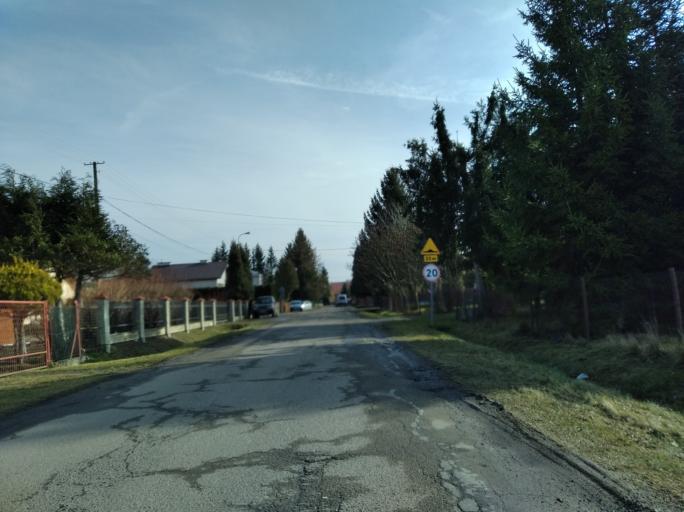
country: PL
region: Subcarpathian Voivodeship
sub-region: Powiat brzozowski
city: Humniska
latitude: 49.6689
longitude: 22.0536
